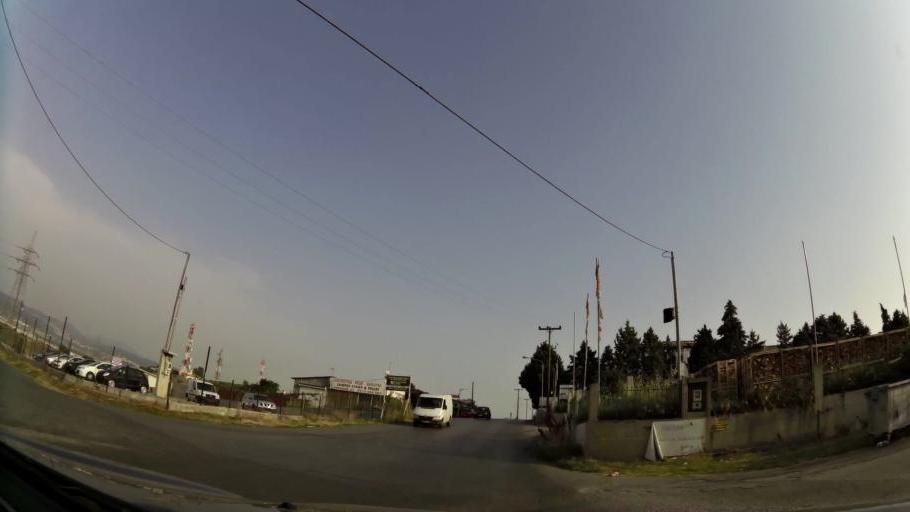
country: GR
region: Central Macedonia
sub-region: Nomos Thessalonikis
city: Evosmos
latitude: 40.6908
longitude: 22.9061
